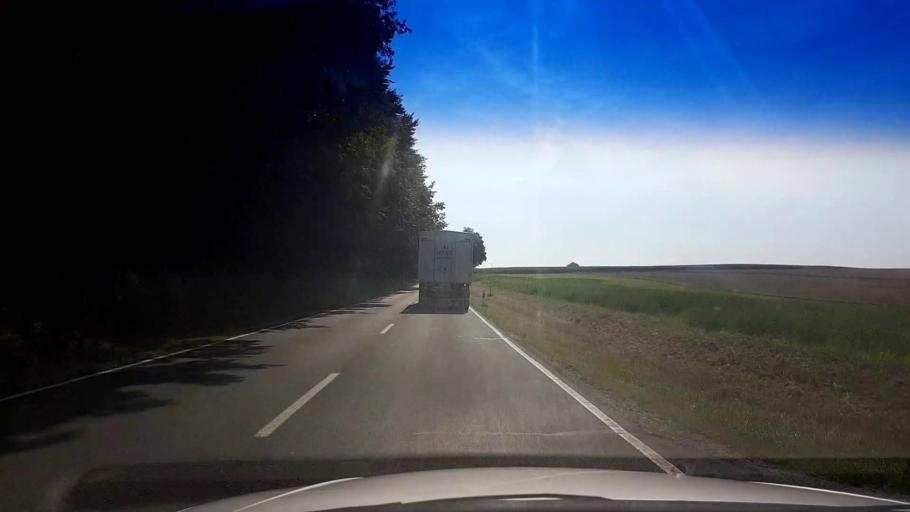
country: DE
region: Bavaria
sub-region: Upper Franconia
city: Hollfeld
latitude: 49.9589
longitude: 11.2679
